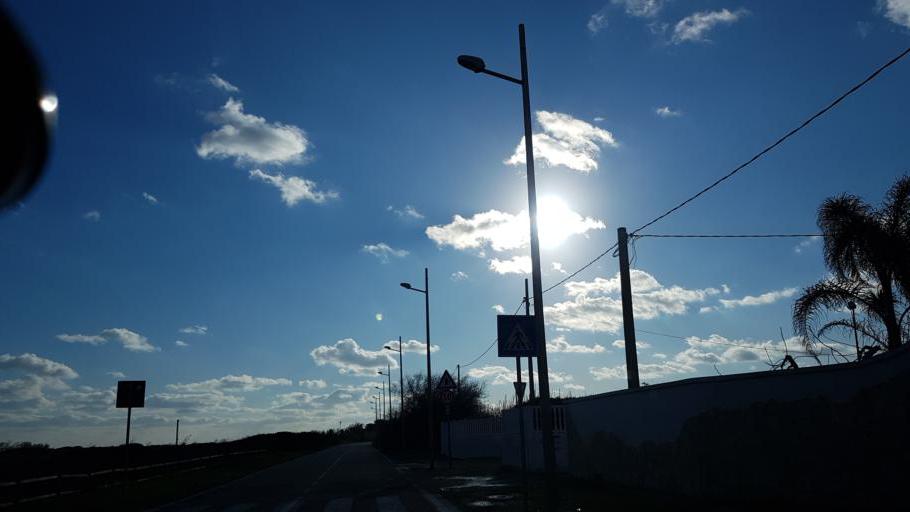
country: IT
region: Apulia
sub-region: Provincia di Brindisi
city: Materdomini
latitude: 40.6770
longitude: 17.9418
